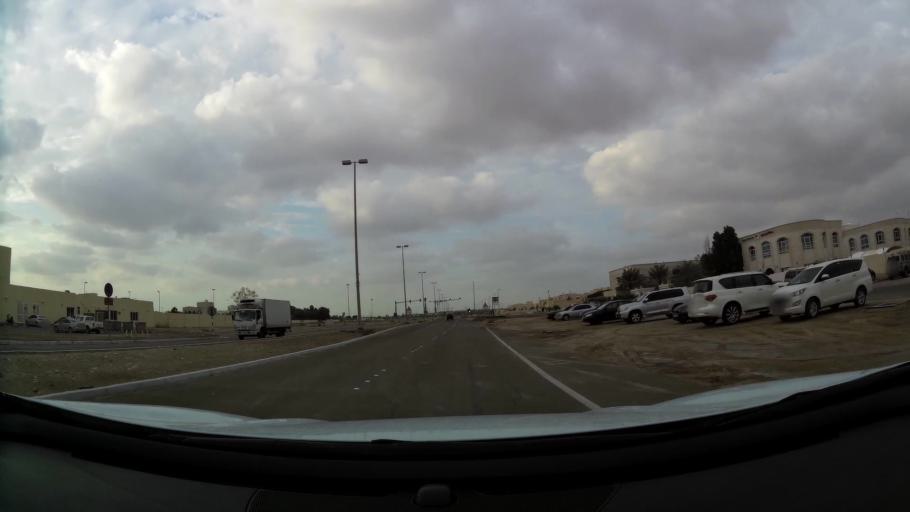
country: AE
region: Abu Dhabi
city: Abu Dhabi
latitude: 24.3775
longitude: 54.5362
